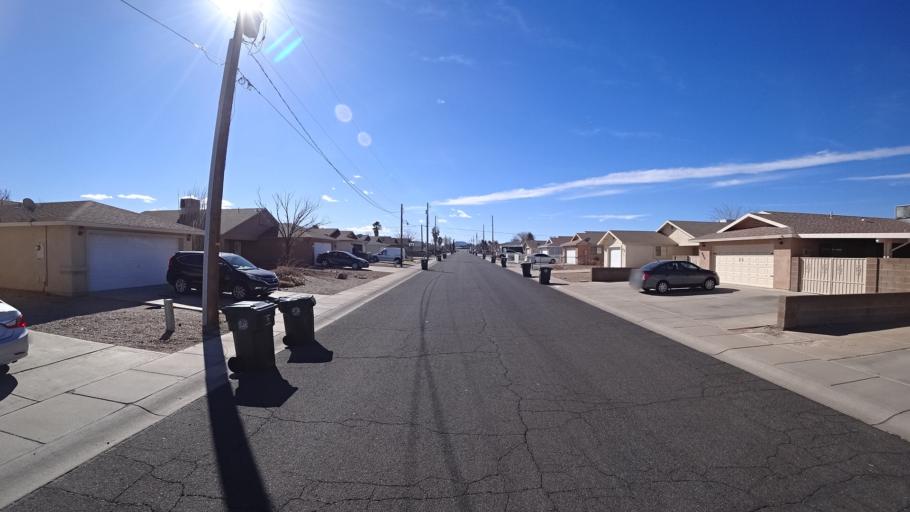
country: US
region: Arizona
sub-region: Mohave County
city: New Kingman-Butler
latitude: 35.2294
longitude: -114.0259
